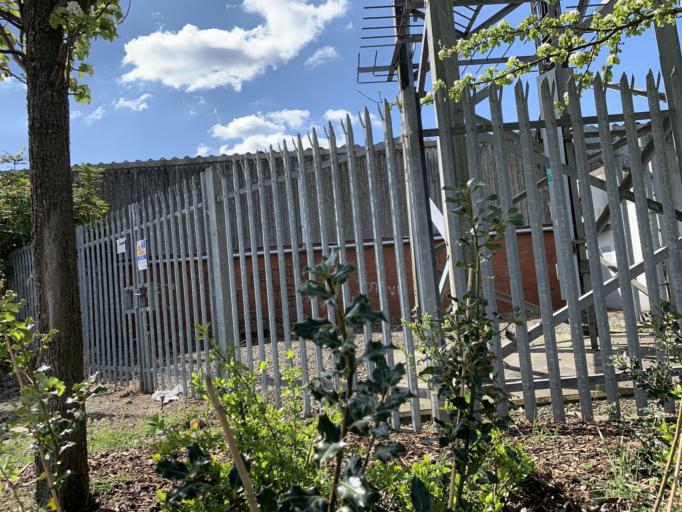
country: GB
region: Scotland
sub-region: Glasgow City
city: Glasgow
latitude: 55.8715
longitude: -4.2488
